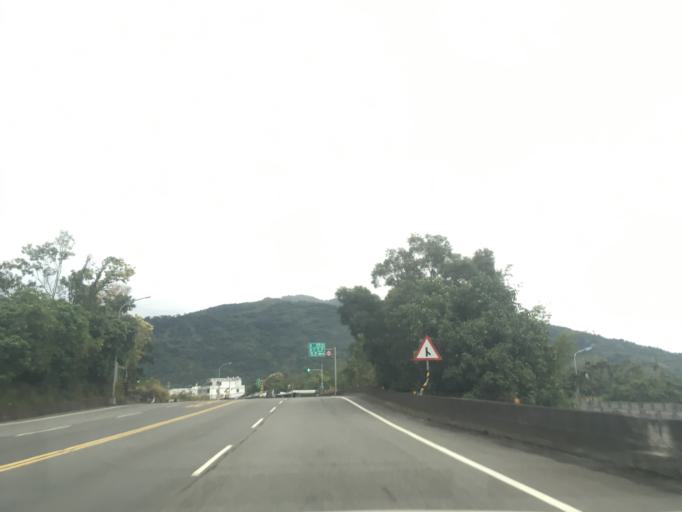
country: TW
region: Taiwan
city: Taitung City
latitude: 22.7551
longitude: 121.0532
